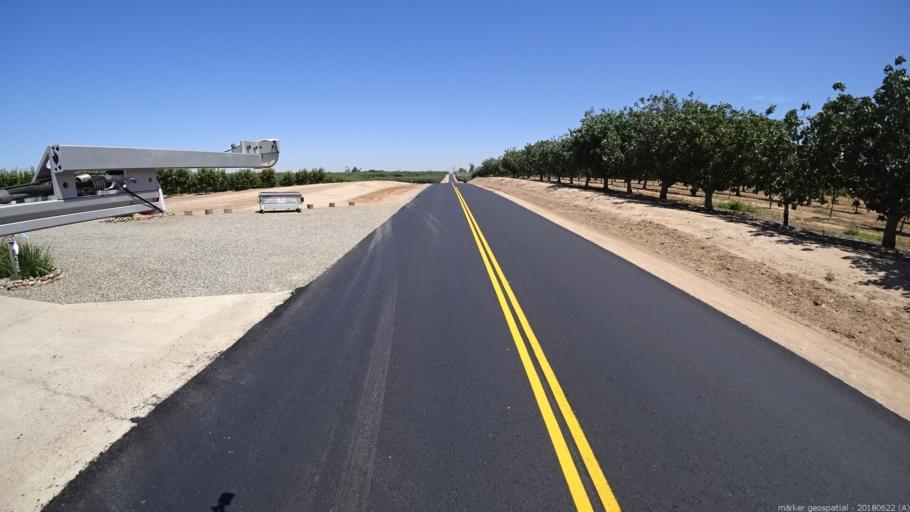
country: US
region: California
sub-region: Madera County
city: Bonadelle Ranchos-Madera Ranchos
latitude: 36.9058
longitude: -119.8577
